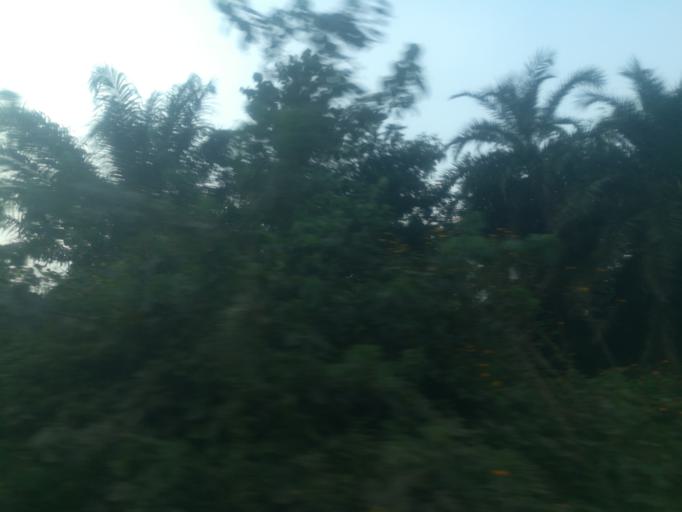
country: NG
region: Ogun
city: Abeokuta
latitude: 7.1457
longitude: 3.2560
